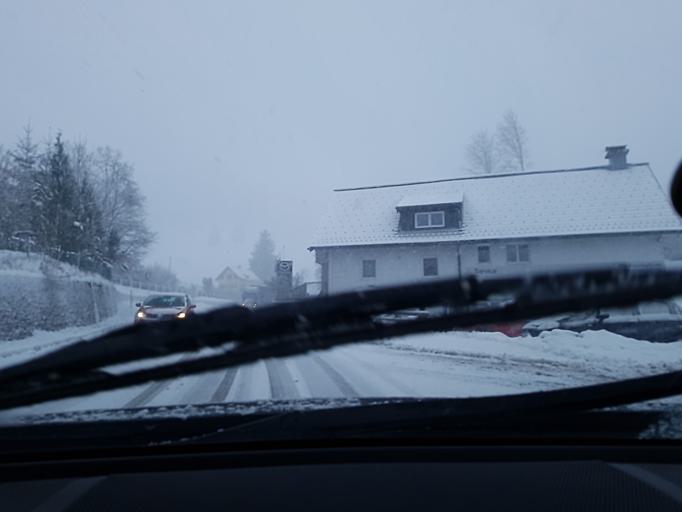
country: AT
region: Salzburg
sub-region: Politischer Bezirk Hallein
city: Abtenau
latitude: 47.5632
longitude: 13.3794
